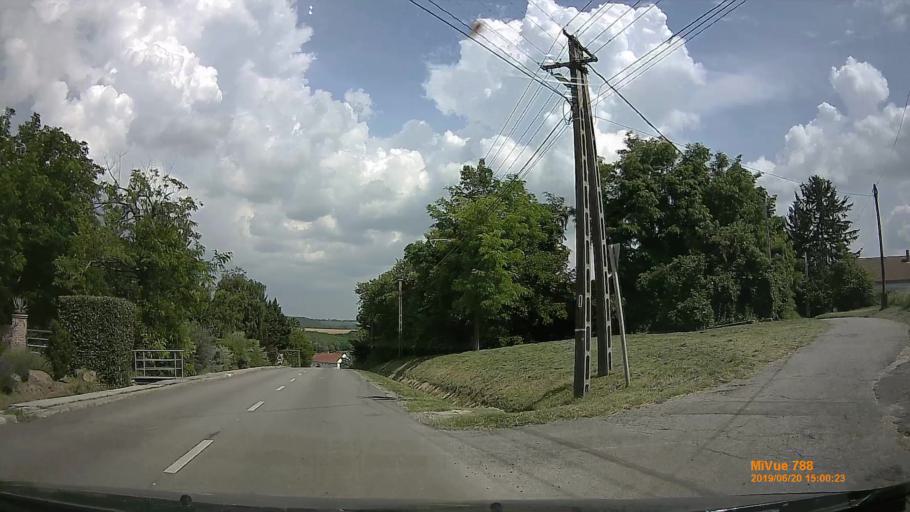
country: HU
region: Baranya
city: Kozarmisleny
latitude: 45.9854
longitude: 18.2574
